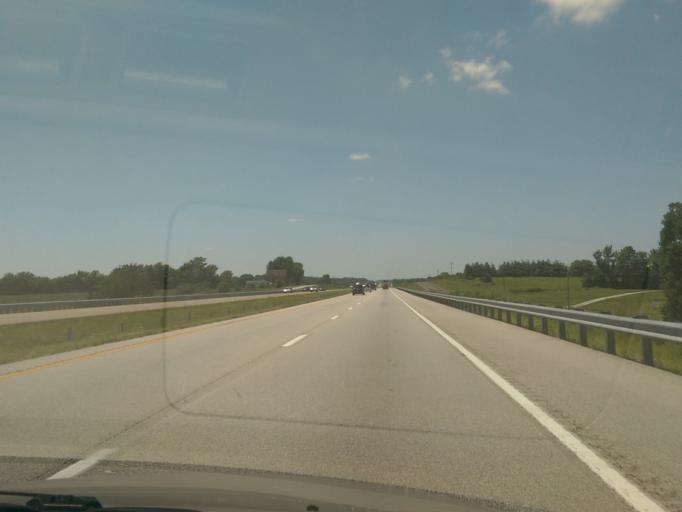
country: US
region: Missouri
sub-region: Cooper County
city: Boonville
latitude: 38.9353
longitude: -92.8563
